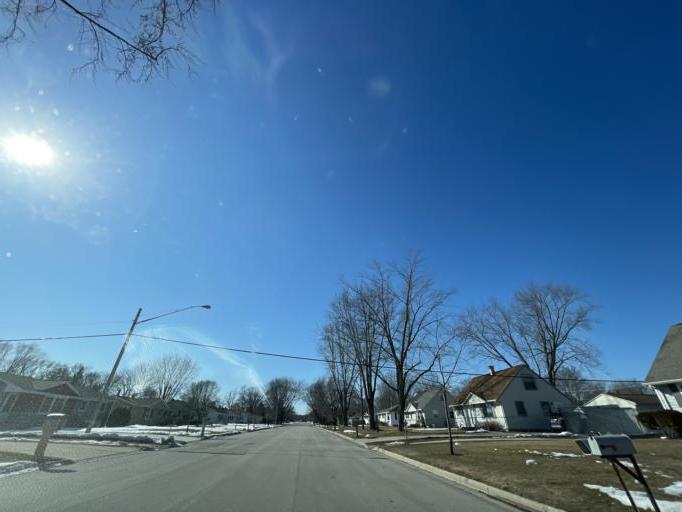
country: US
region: Wisconsin
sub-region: Brown County
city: Howard
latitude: 44.5685
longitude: -88.0821
